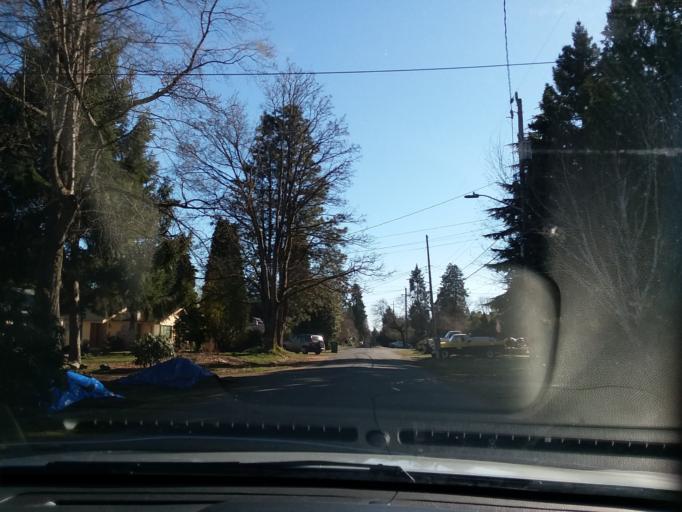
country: US
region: Washington
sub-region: King County
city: Shoreline
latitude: 47.7296
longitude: -122.3316
